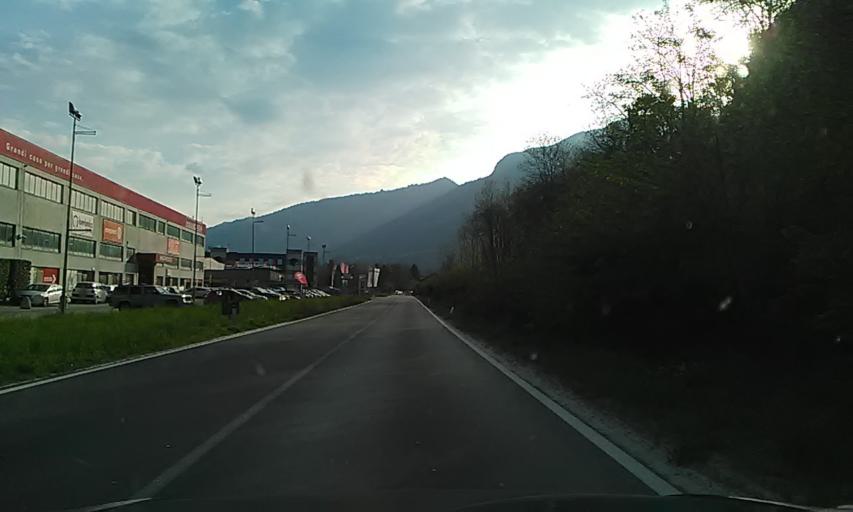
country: IT
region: Piedmont
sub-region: Provincia Verbano-Cusio-Ossola
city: Mergozzo
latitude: 45.9399
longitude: 8.4637
